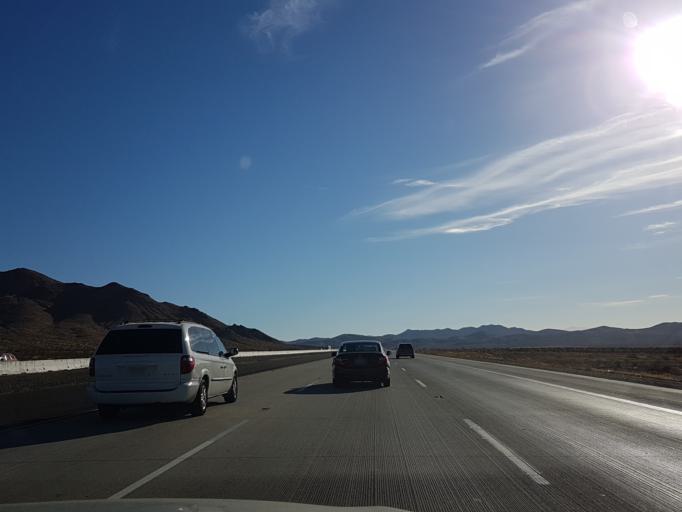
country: US
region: California
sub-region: San Bernardino County
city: Lenwood
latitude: 34.7371
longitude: -117.1813
